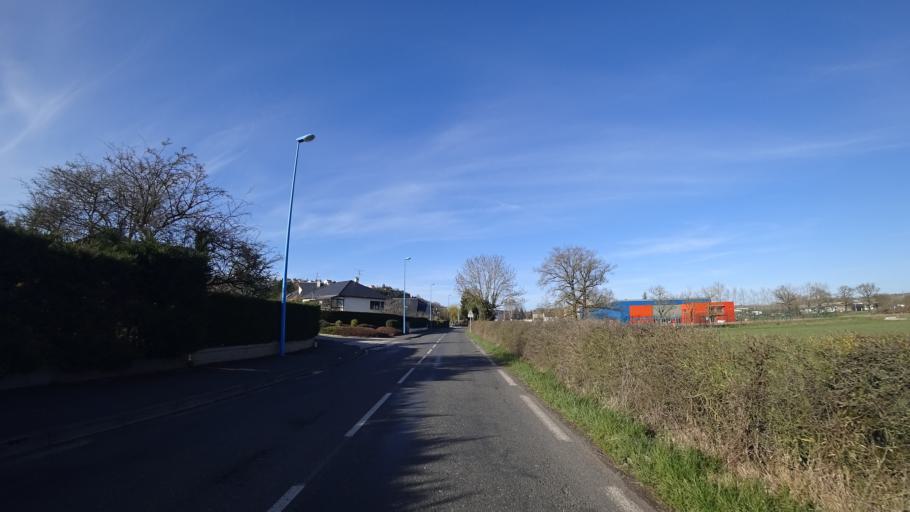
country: FR
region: Midi-Pyrenees
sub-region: Departement de l'Aveyron
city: Rodez
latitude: 44.3709
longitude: 2.5761
